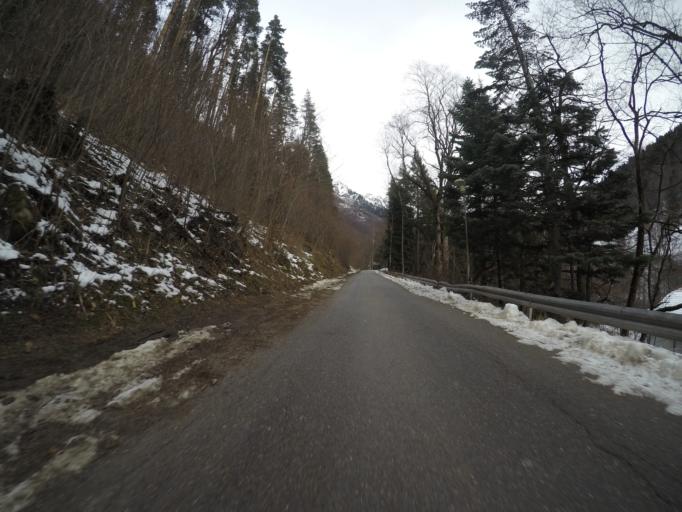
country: BG
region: Kyustendil
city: Sapareva Banya
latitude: 42.1352
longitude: 23.3421
